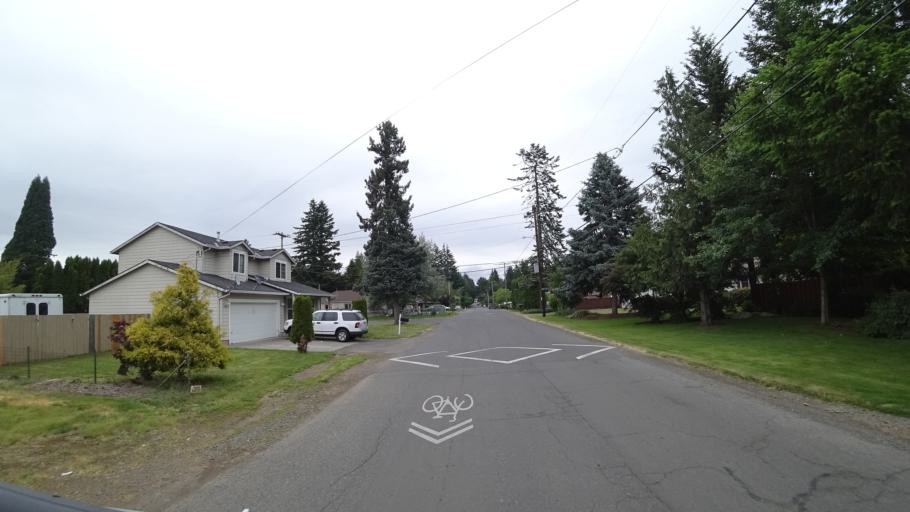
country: US
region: Oregon
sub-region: Clackamas County
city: Happy Valley
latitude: 45.4951
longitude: -122.5150
